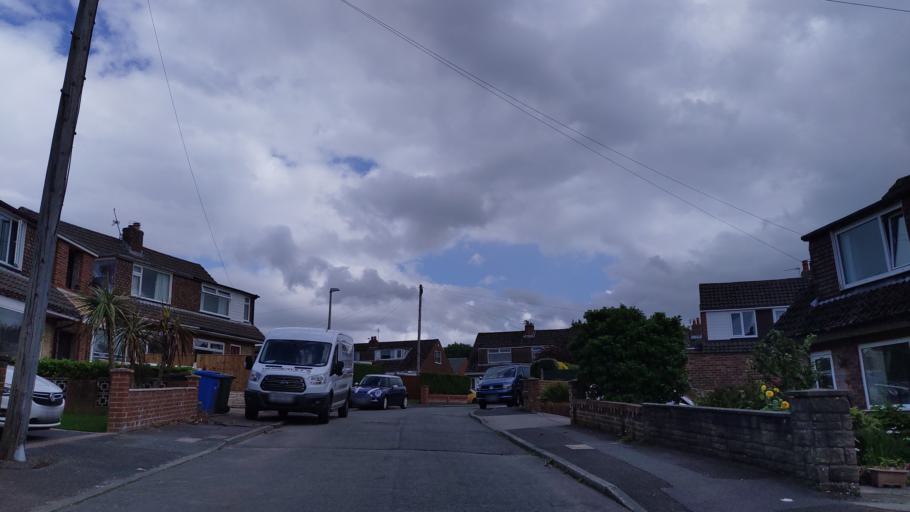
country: GB
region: England
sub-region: Lancashire
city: Coppull
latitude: 53.6489
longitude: -2.6458
